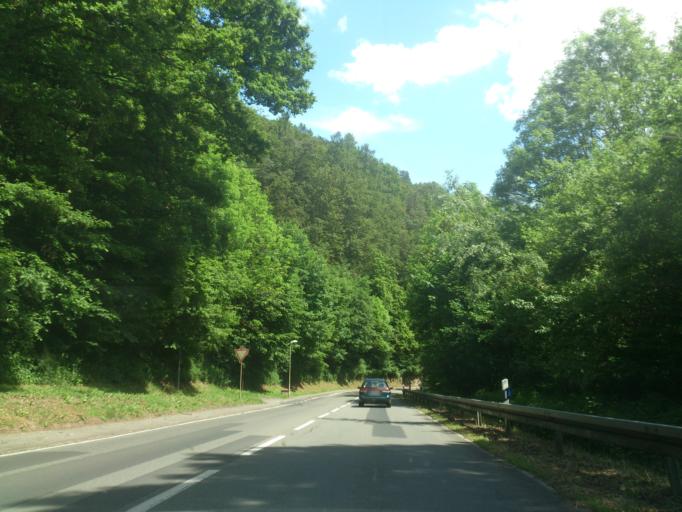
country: DE
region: Lower Saxony
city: Bad Karlshafen
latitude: 51.6322
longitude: 9.4474
